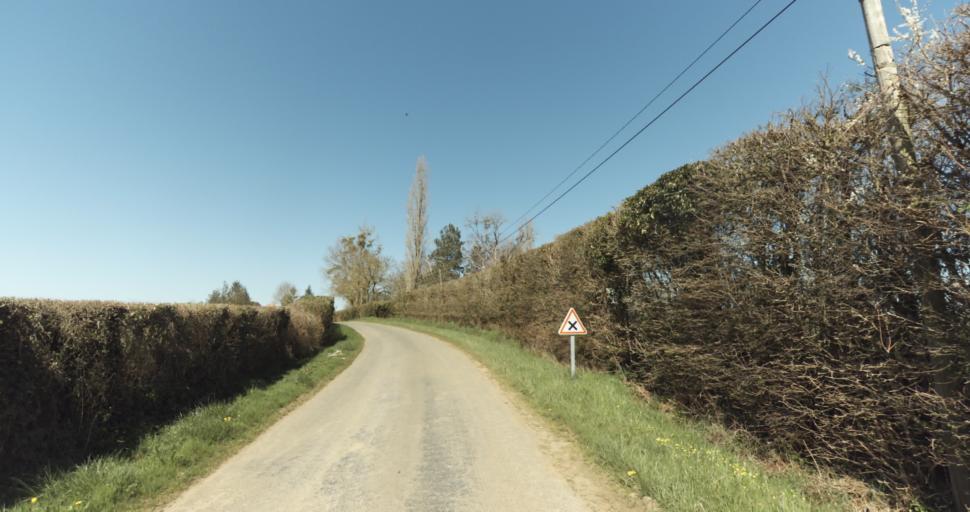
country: FR
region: Lower Normandy
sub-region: Departement du Calvados
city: Saint-Pierre-sur-Dives
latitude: 49.0098
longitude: 0.0160
